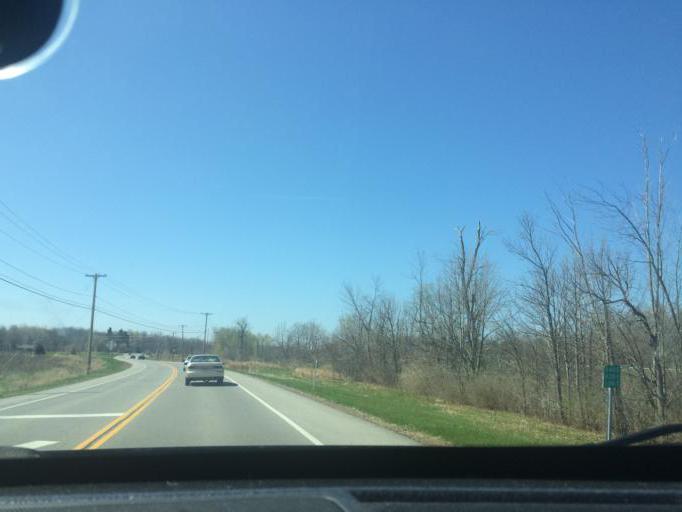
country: US
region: New York
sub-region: Monroe County
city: North Gates
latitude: 43.0968
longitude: -77.6774
